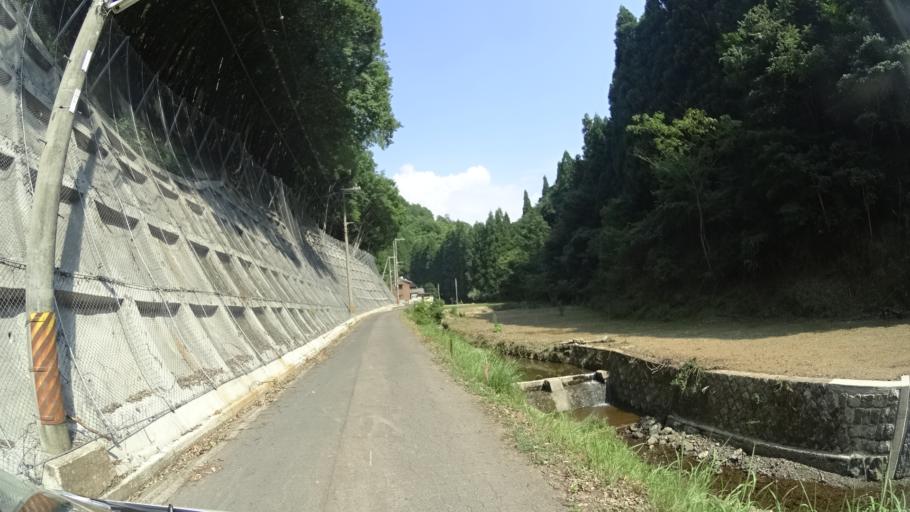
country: JP
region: Kyoto
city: Maizuru
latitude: 35.4094
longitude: 135.2316
